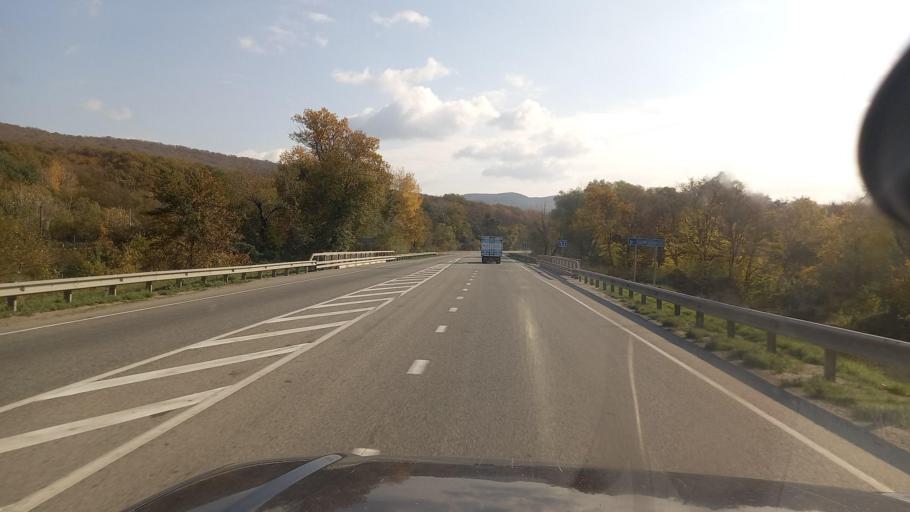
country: RU
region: Krasnodarskiy
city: Verkhnebakanskiy
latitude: 44.8434
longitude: 37.6932
